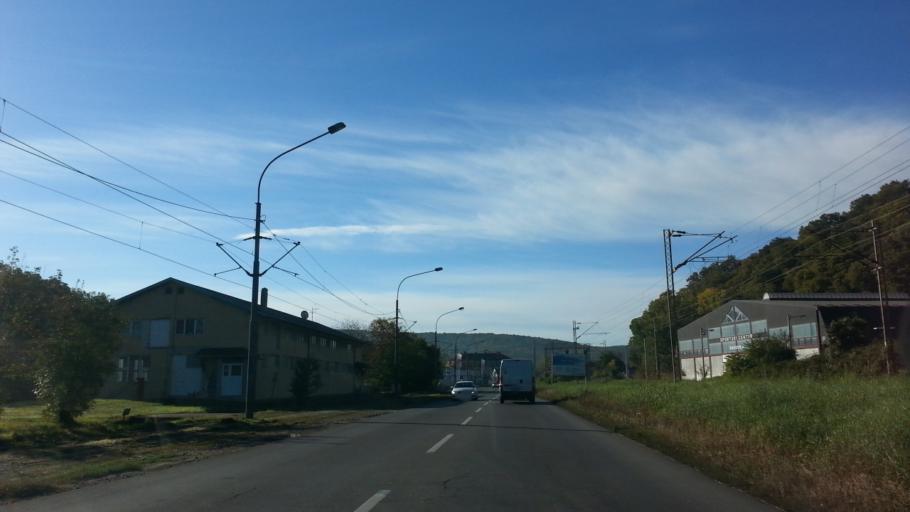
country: RS
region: Central Serbia
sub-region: Belgrade
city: Rakovica
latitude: 44.7538
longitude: 20.4460
